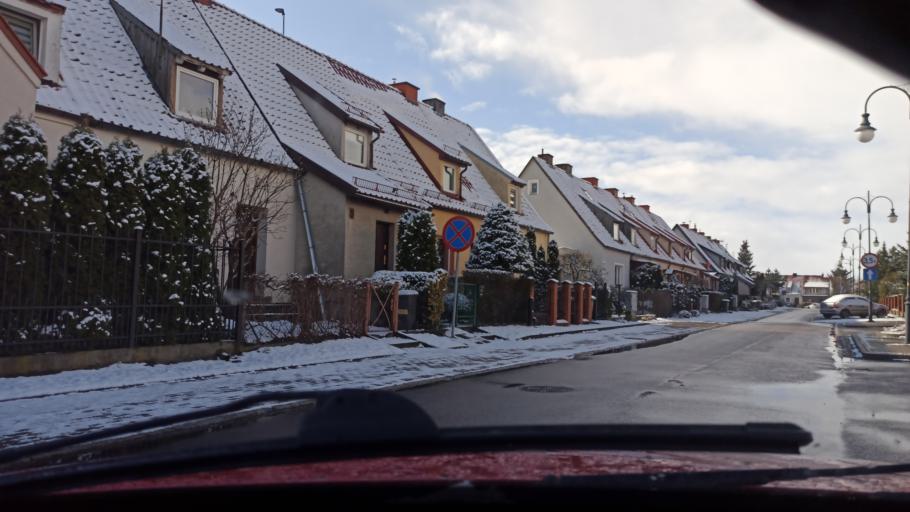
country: PL
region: Warmian-Masurian Voivodeship
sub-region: Powiat elblaski
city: Elblag
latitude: 54.1449
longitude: 19.4073
